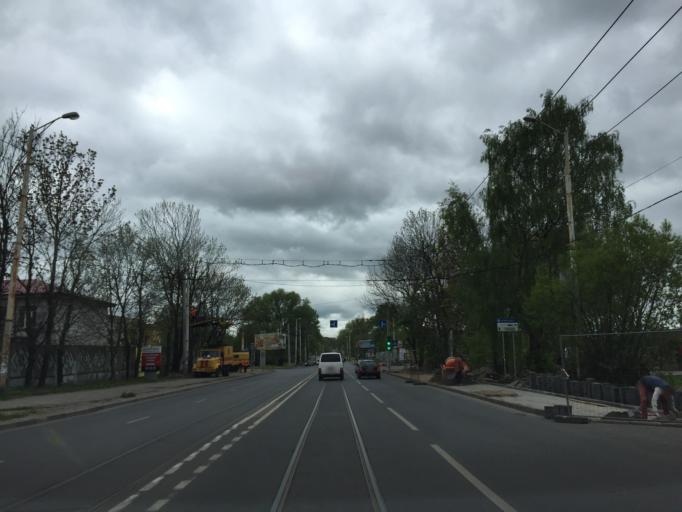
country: RU
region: Kaliningrad
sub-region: Gorod Kaliningrad
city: Kaliningrad
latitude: 54.6913
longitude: 20.4677
